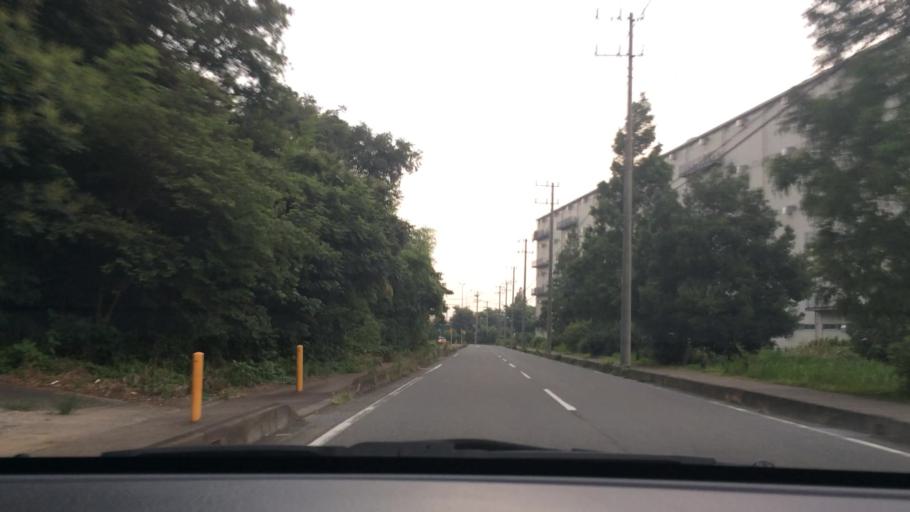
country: JP
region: Chiba
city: Nagareyama
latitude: 35.8814
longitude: 139.9013
